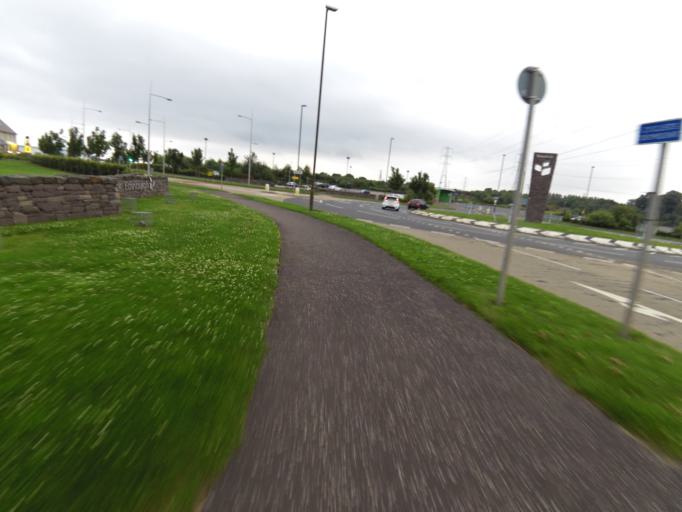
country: GB
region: Scotland
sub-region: Midlothian
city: Bonnyrigg
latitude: 55.9055
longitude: -3.1013
